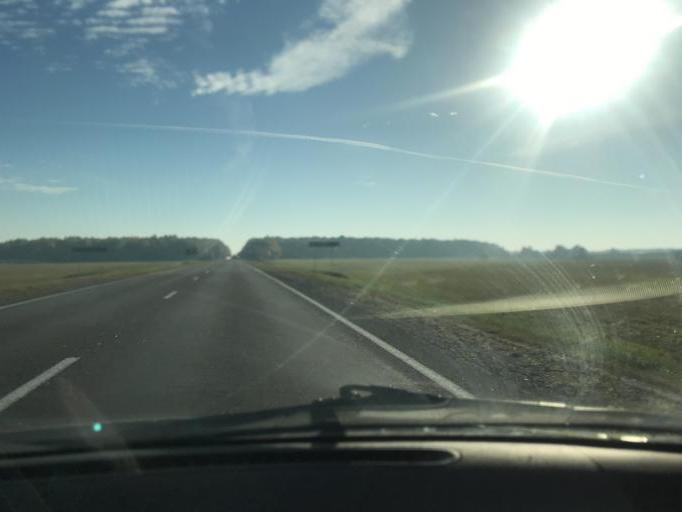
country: BY
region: Brest
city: Drahichyn
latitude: 52.1544
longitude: 25.3458
